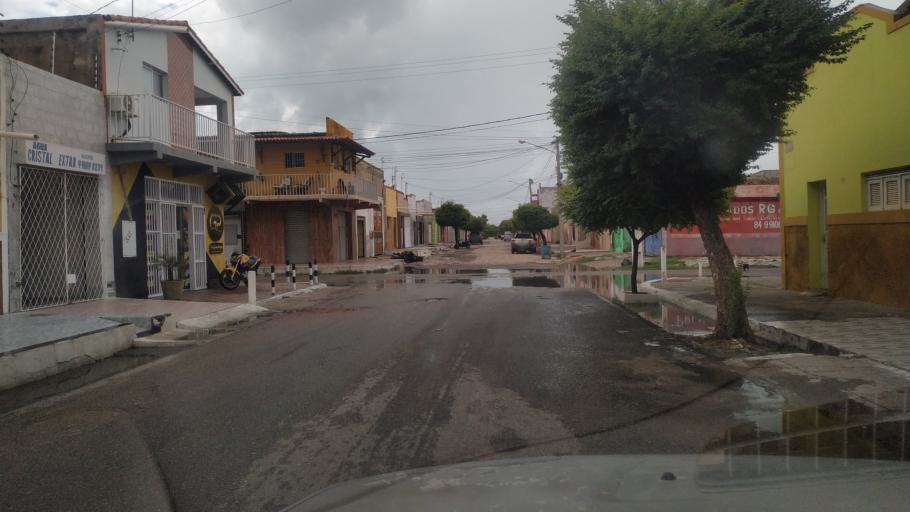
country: BR
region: Rio Grande do Norte
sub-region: Areia Branca
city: Areia Branca
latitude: -4.9535
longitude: -37.1351
